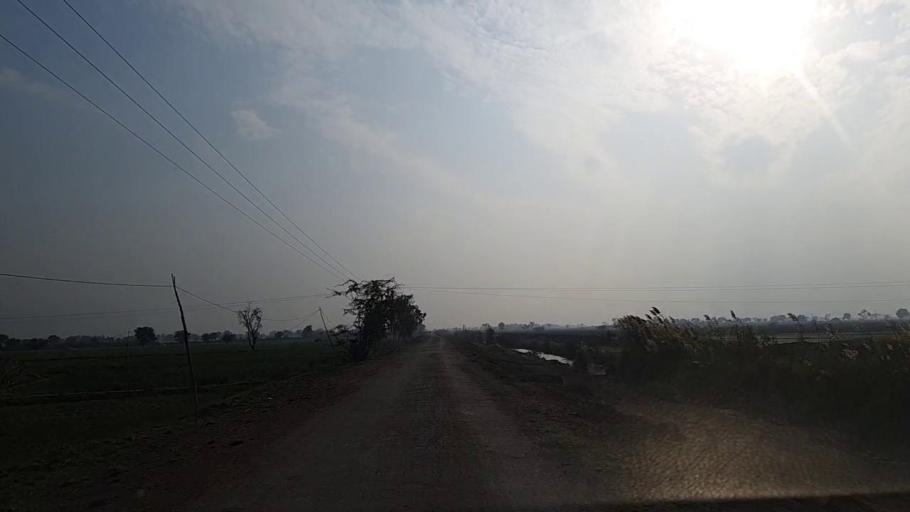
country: PK
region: Sindh
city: Jam Sahib
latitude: 26.3138
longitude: 68.5249
